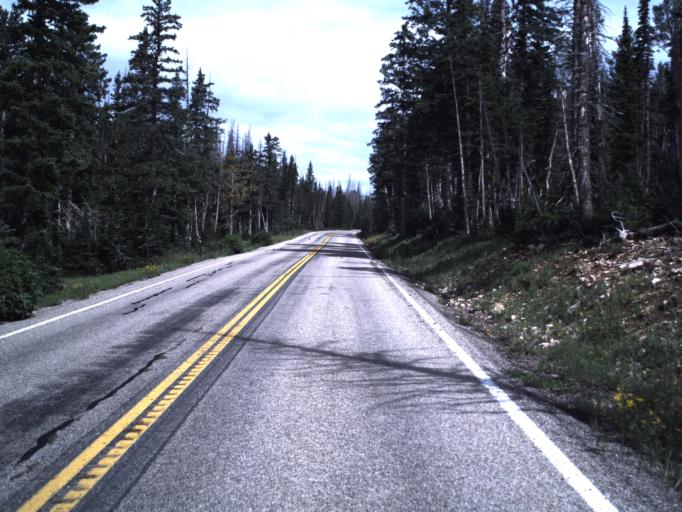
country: US
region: Utah
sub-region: Iron County
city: Cedar City
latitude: 37.5817
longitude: -112.8447
